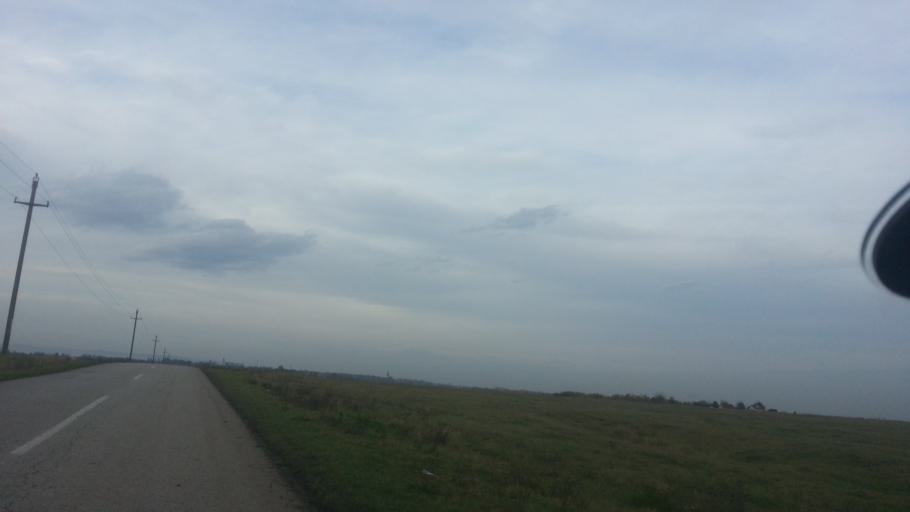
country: RS
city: Putinci
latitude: 44.9689
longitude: 19.9737
